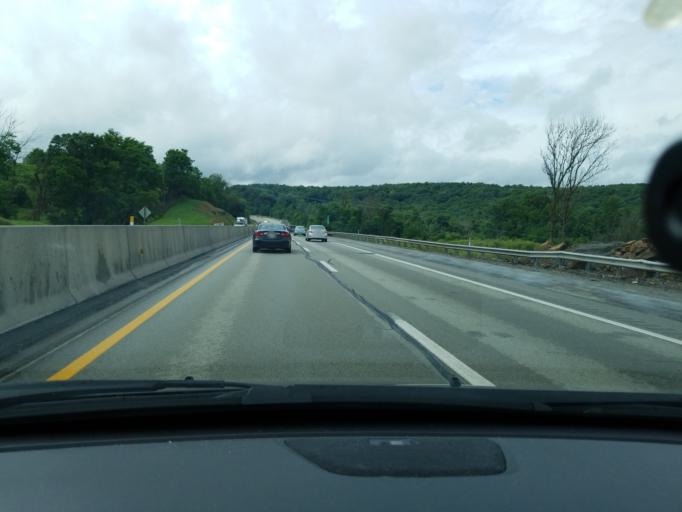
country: US
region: Pennsylvania
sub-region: Somerset County
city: Somerset
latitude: 40.0477
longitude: -79.1224
